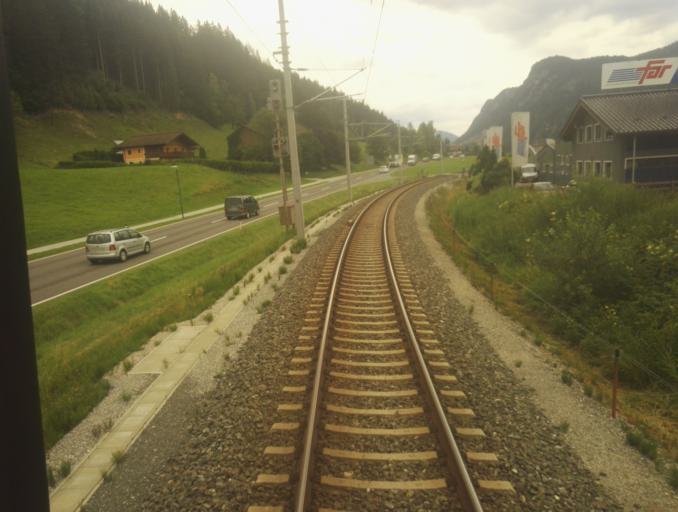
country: AT
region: Salzburg
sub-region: Politischer Bezirk Sankt Johann im Pongau
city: Radstadt
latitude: 47.3863
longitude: 13.4762
